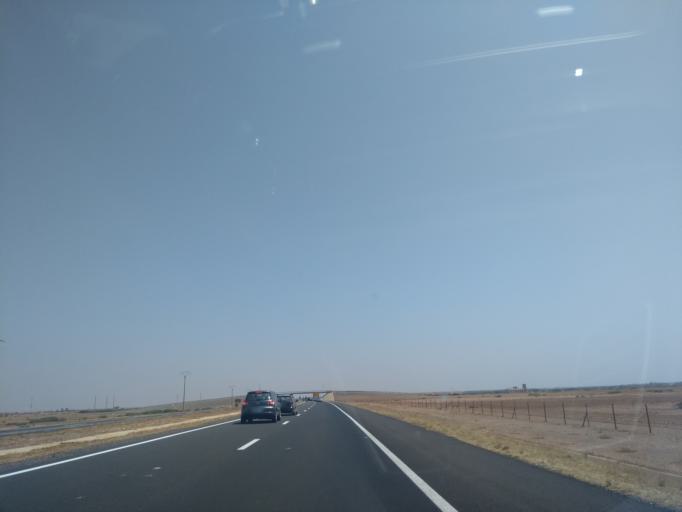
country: MA
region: Marrakech-Tensift-Al Haouz
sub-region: Kelaa-Des-Sraghna
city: Sidi Bou Othmane
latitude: 31.9320
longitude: -8.0184
